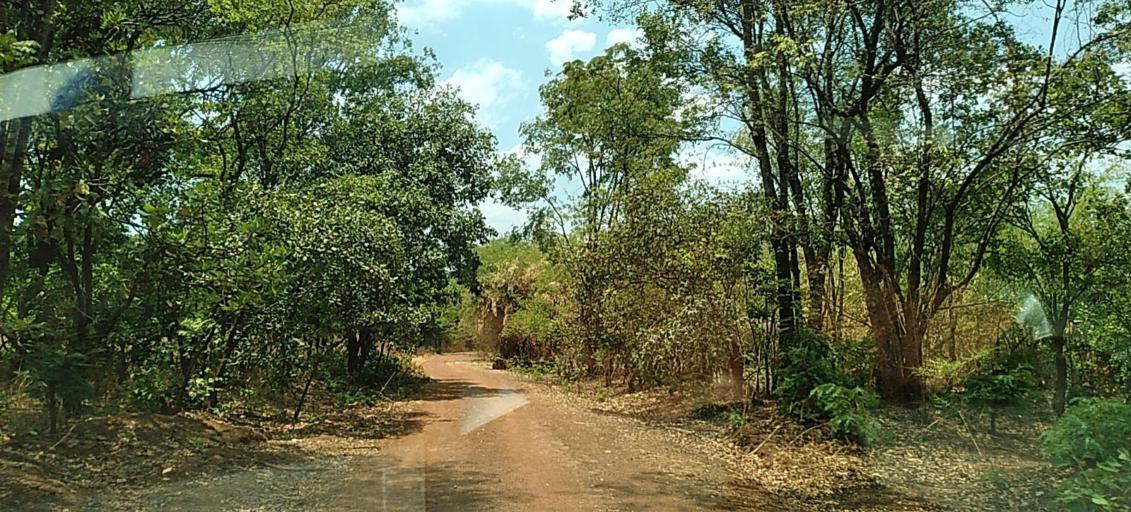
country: ZM
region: Copperbelt
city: Chingola
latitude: -12.5451
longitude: 27.6317
